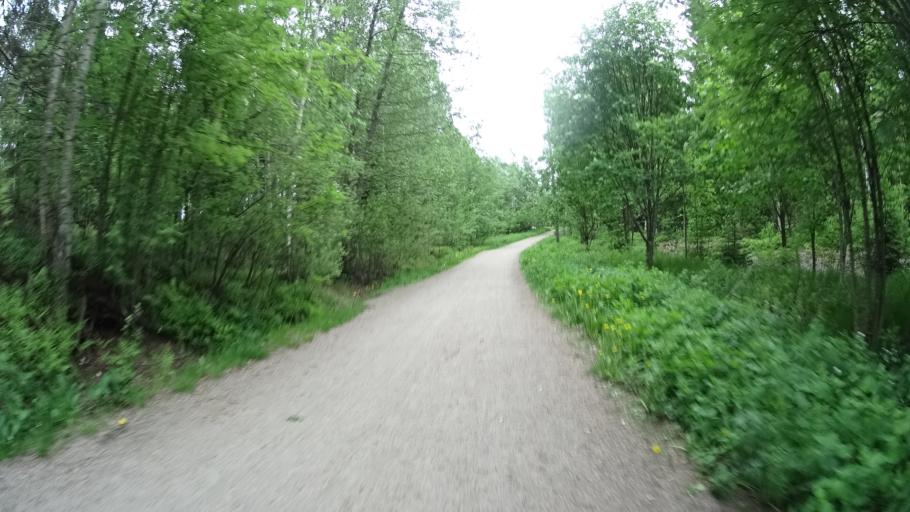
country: FI
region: Uusimaa
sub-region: Helsinki
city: Vantaa
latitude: 60.2484
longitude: 25.0748
